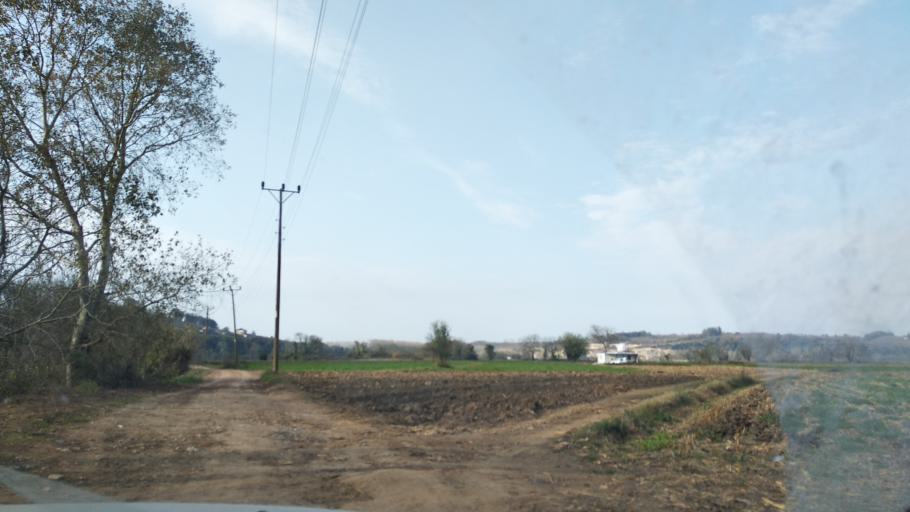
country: TR
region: Sakarya
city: Karasu
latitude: 41.0868
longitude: 30.6008
